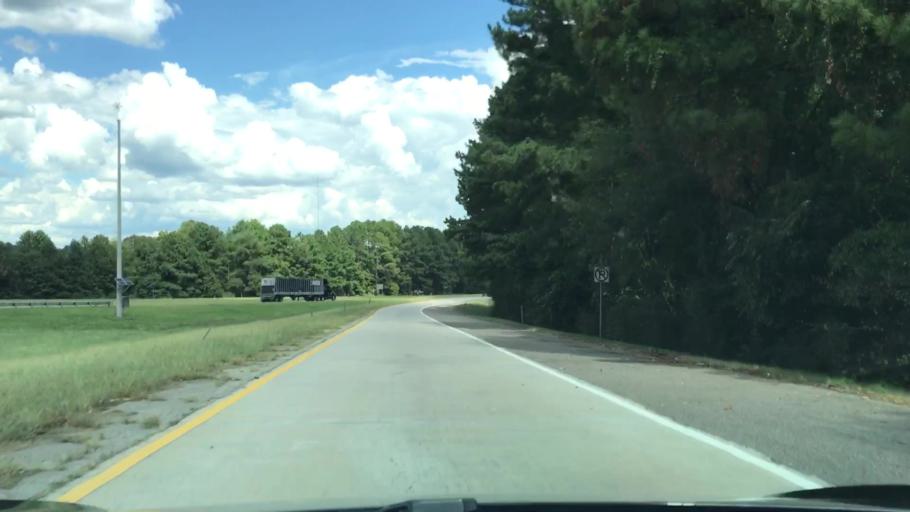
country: US
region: Georgia
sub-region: Greene County
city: Union Point
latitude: 33.5432
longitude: -83.0783
